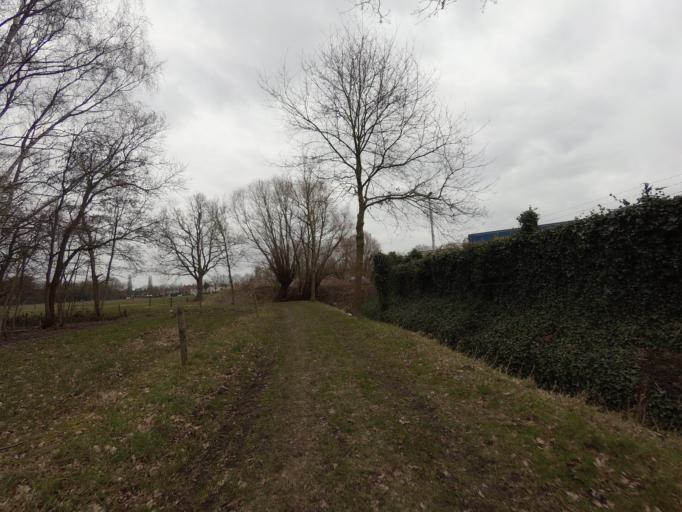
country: BE
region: Flanders
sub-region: Provincie Antwerpen
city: Aartselaar
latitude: 51.1370
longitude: 4.3717
